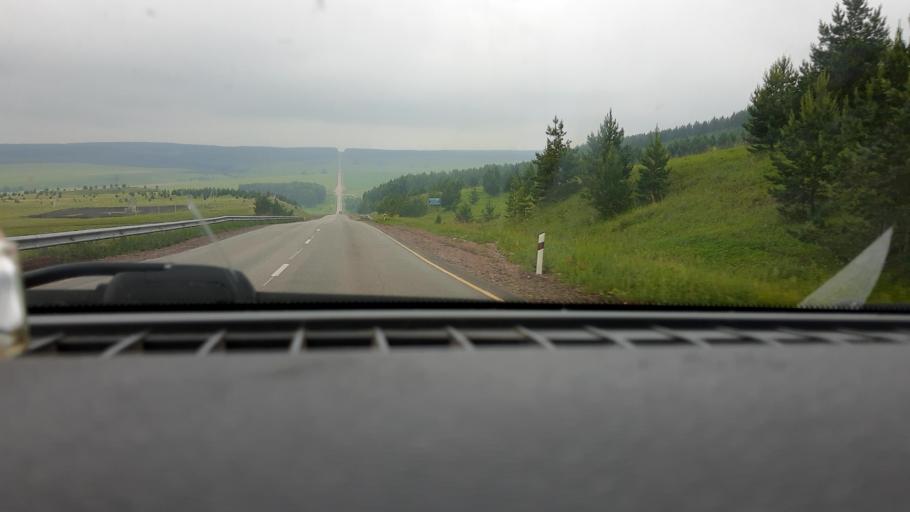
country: RU
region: Bashkortostan
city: Belebey
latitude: 54.2634
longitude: 54.0688
